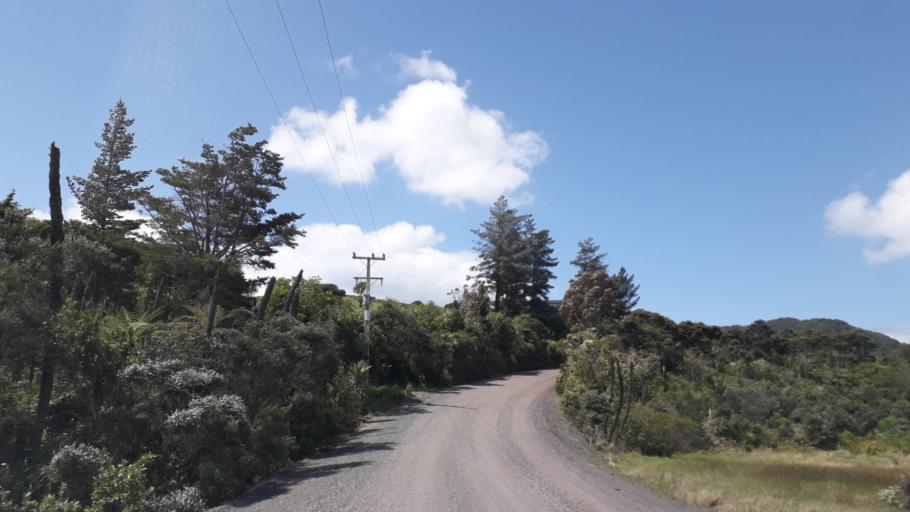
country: NZ
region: Northland
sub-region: Far North District
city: Paihia
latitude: -35.2382
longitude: 174.2499
